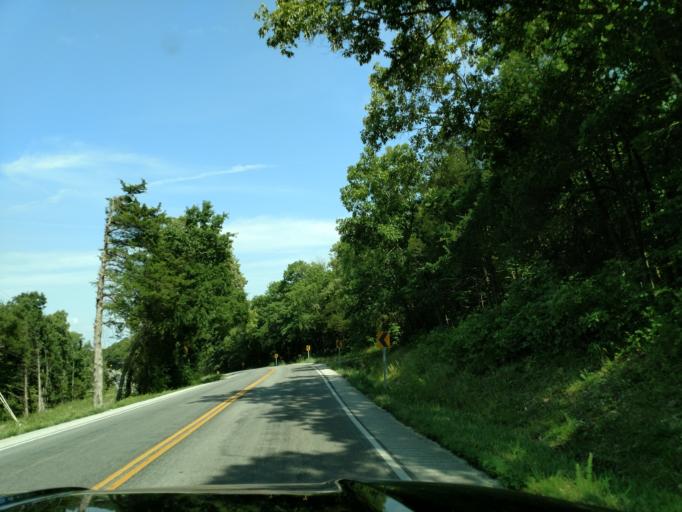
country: US
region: Missouri
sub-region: Barry County
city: Shell Knob
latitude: 36.6099
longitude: -93.5886
